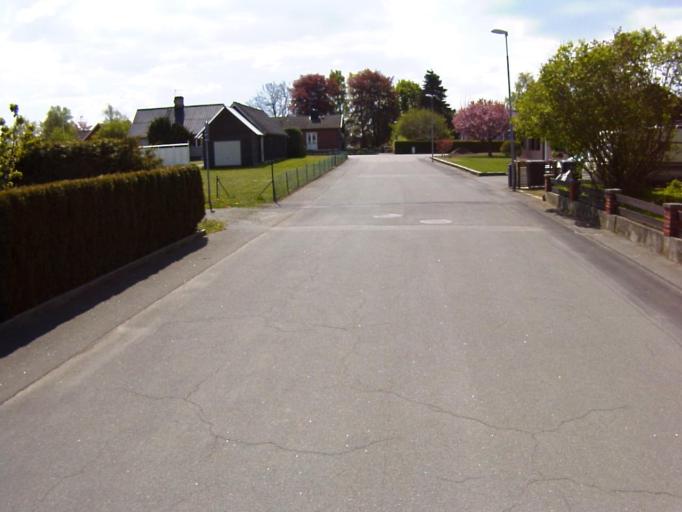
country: SE
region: Skane
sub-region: Kristianstads Kommun
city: Fjalkinge
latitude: 56.0165
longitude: 14.2275
